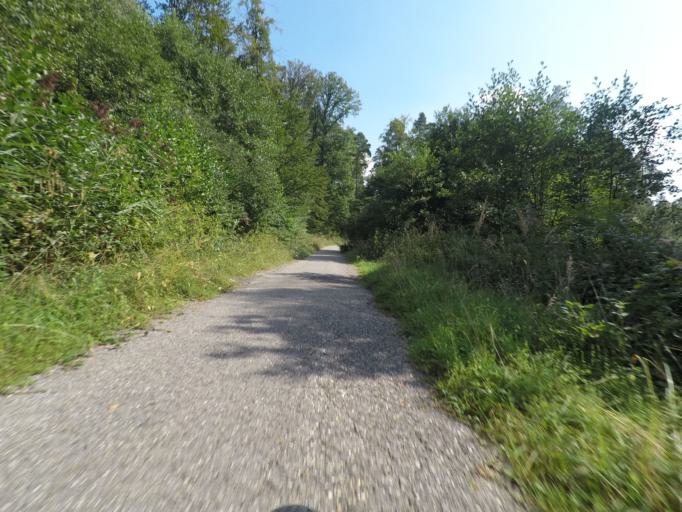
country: DE
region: Baden-Wuerttemberg
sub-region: Regierungsbezirk Stuttgart
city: Steinenbronn
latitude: 48.7066
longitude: 9.0885
